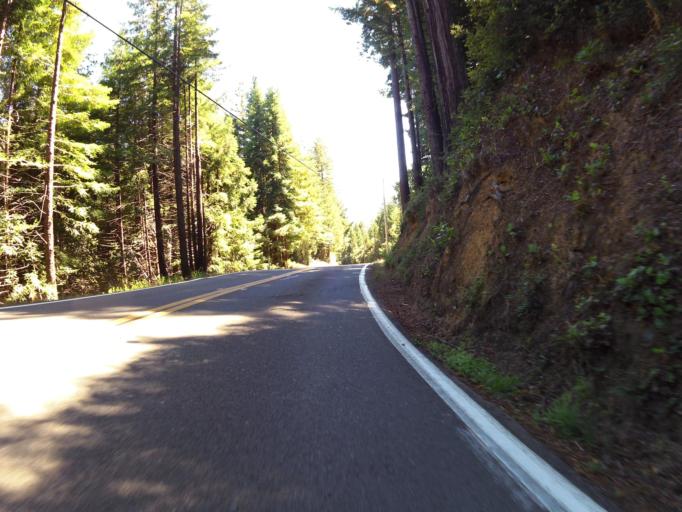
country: US
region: California
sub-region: Mendocino County
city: Fort Bragg
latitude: 39.7226
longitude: -123.8080
